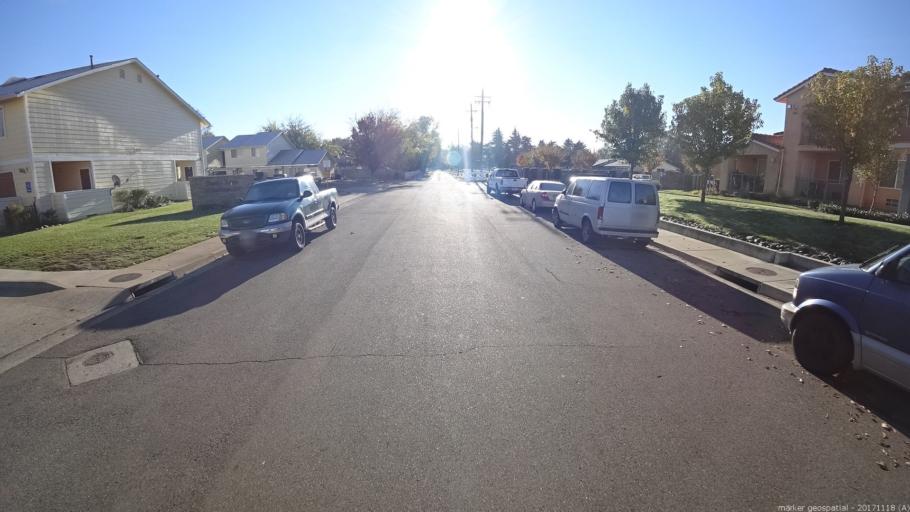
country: US
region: California
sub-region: Shasta County
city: Anderson
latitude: 40.4523
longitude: -122.2837
